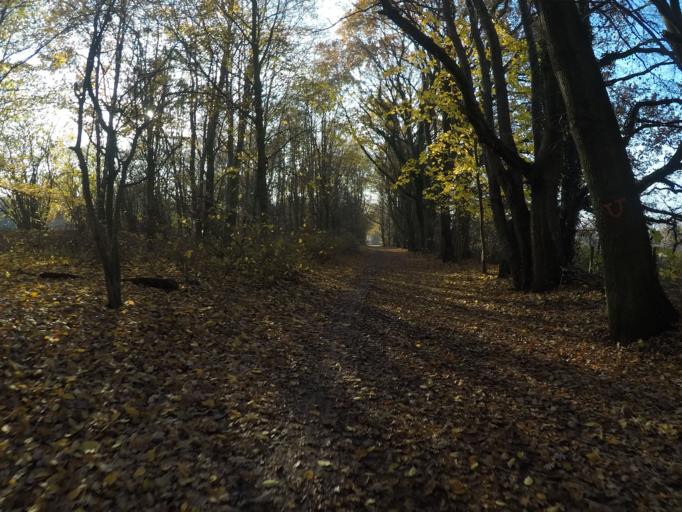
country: DE
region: Hamburg
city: Eidelstedt
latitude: 53.6230
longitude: 9.9252
